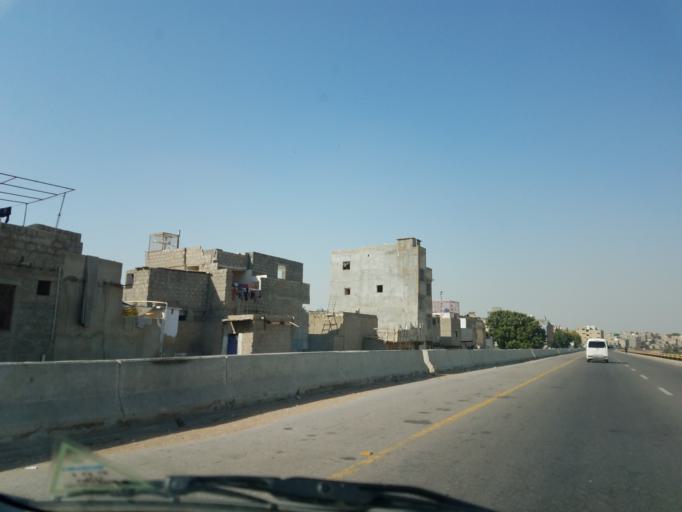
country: PK
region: Sindh
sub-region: Karachi District
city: Karachi
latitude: 24.9199
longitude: 67.0788
